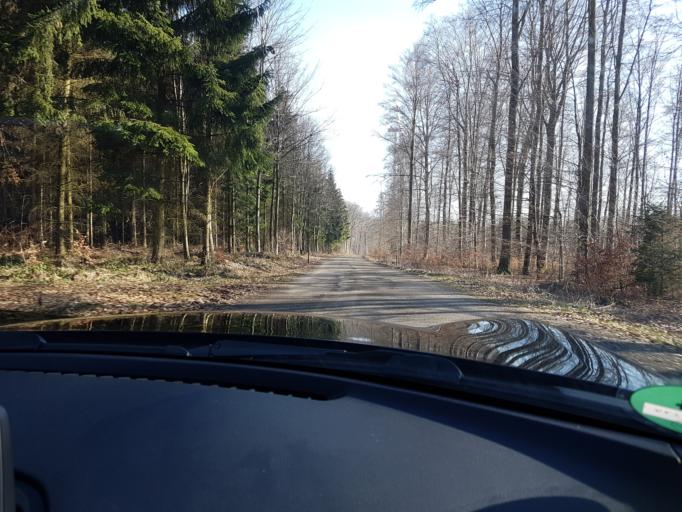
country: DE
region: Baden-Wuerttemberg
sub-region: Regierungsbezirk Stuttgart
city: Langenburg
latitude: 49.2881
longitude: 9.8740
